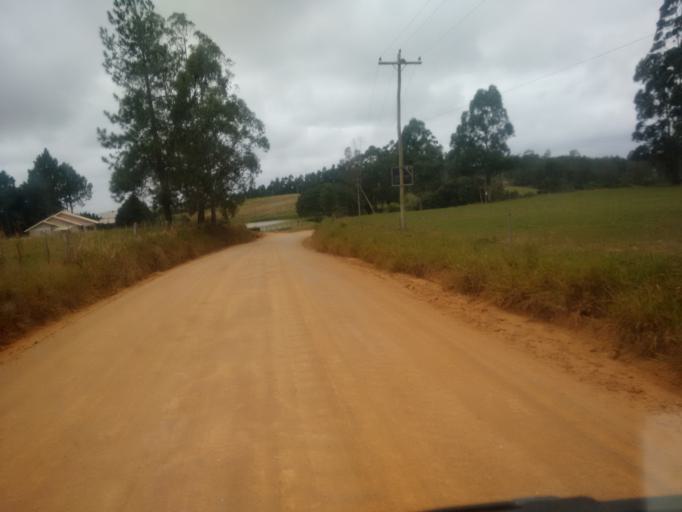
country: BR
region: Rio Grande do Sul
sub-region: Camaqua
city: Camaqua
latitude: -30.7980
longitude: -51.8303
